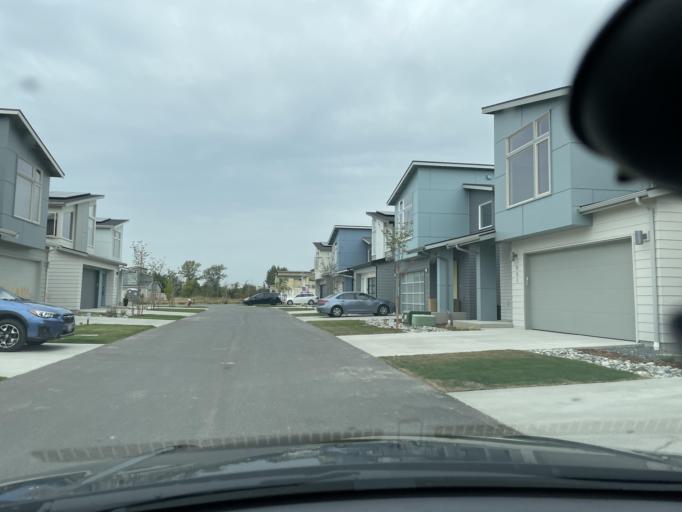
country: US
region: Washington
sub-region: Whatcom County
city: Marietta-Alderwood
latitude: 48.8167
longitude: -122.5056
